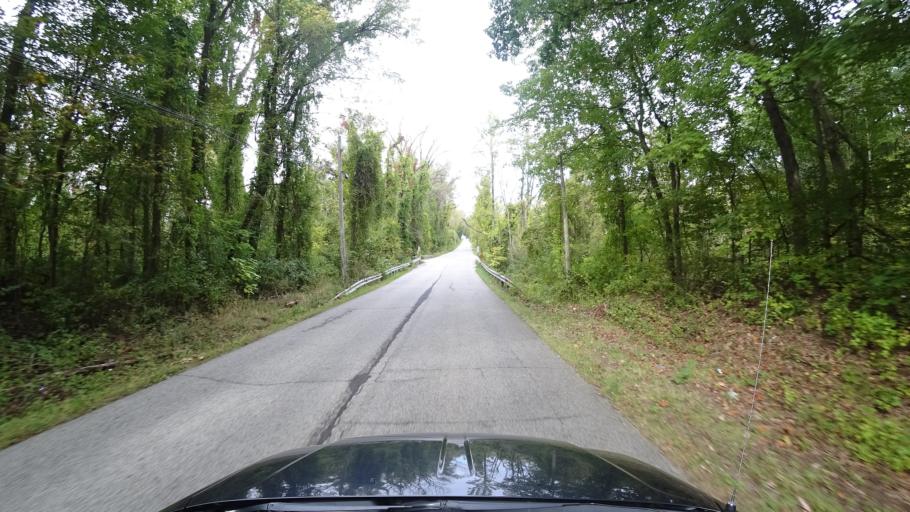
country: US
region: Indiana
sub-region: LaPorte County
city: Trail Creek
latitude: 41.6909
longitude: -86.8163
